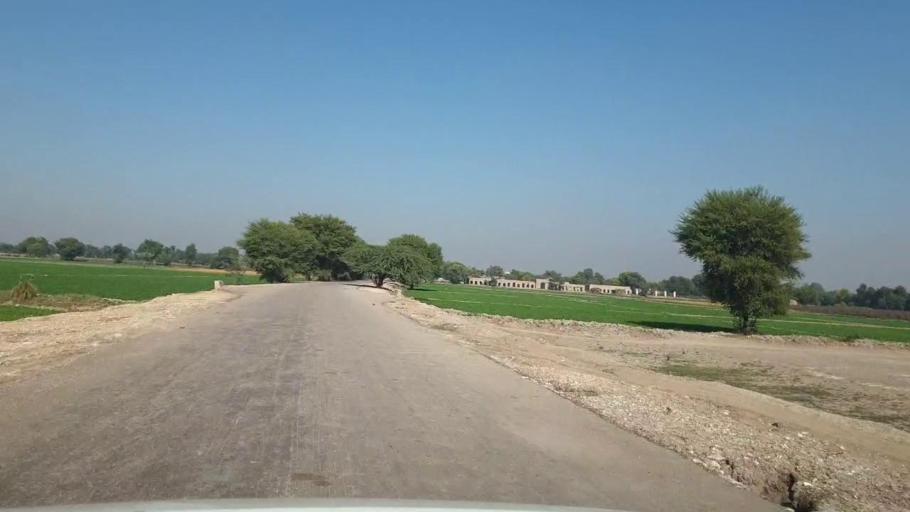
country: PK
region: Sindh
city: Johi
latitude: 26.6630
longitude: 67.7054
